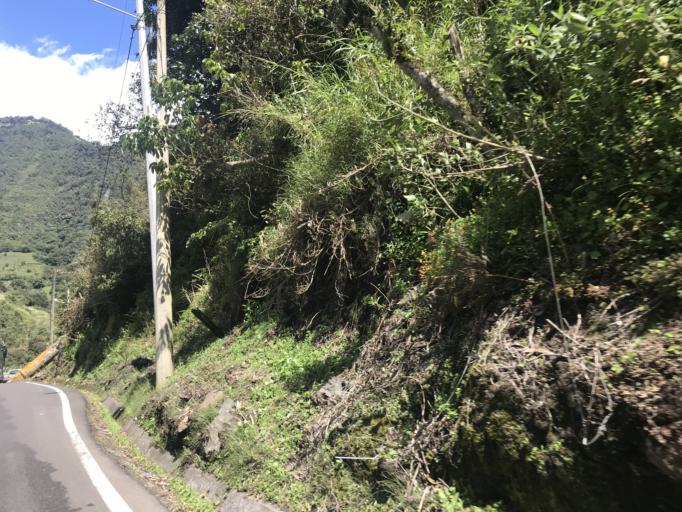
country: EC
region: Tungurahua
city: Banos
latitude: -1.4061
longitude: -78.4057
